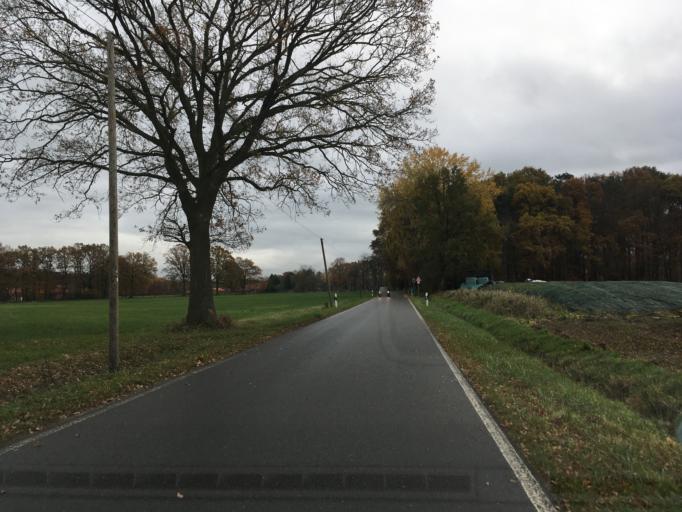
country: DE
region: North Rhine-Westphalia
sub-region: Regierungsbezirk Munster
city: Gescher
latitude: 51.9824
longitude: 6.9896
